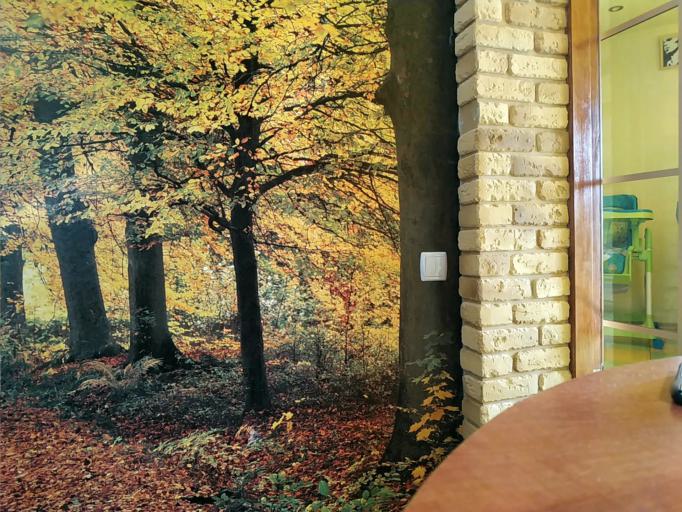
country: RU
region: Novgorod
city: Parfino
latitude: 57.8019
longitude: 31.6066
